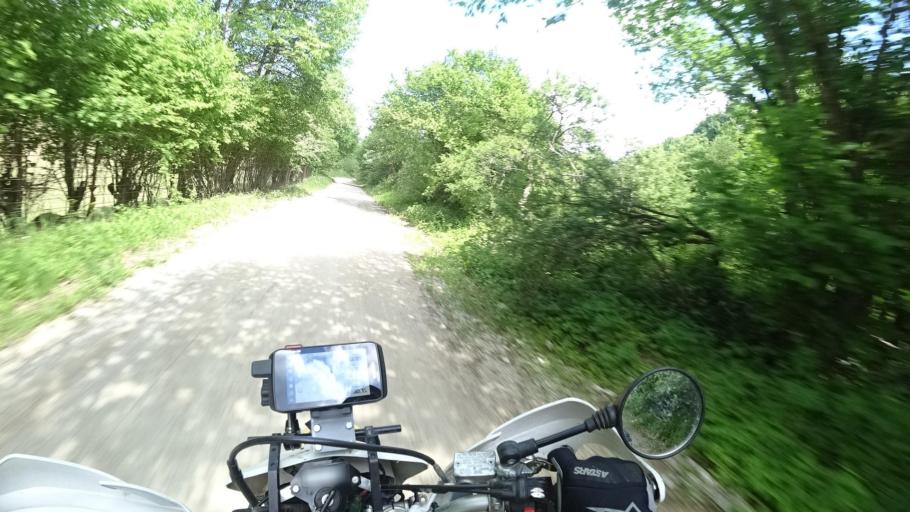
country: BA
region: Federation of Bosnia and Herzegovina
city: Ostrozac
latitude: 44.8353
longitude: 16.0008
